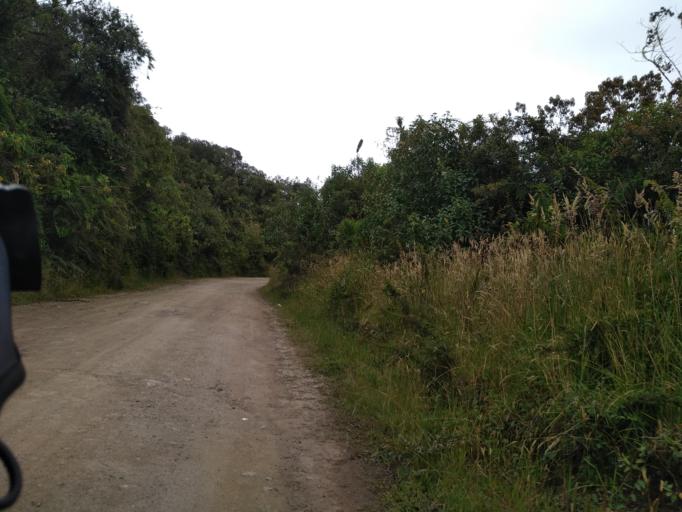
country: EC
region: Carchi
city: Tulcan
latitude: 0.7412
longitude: -77.7871
